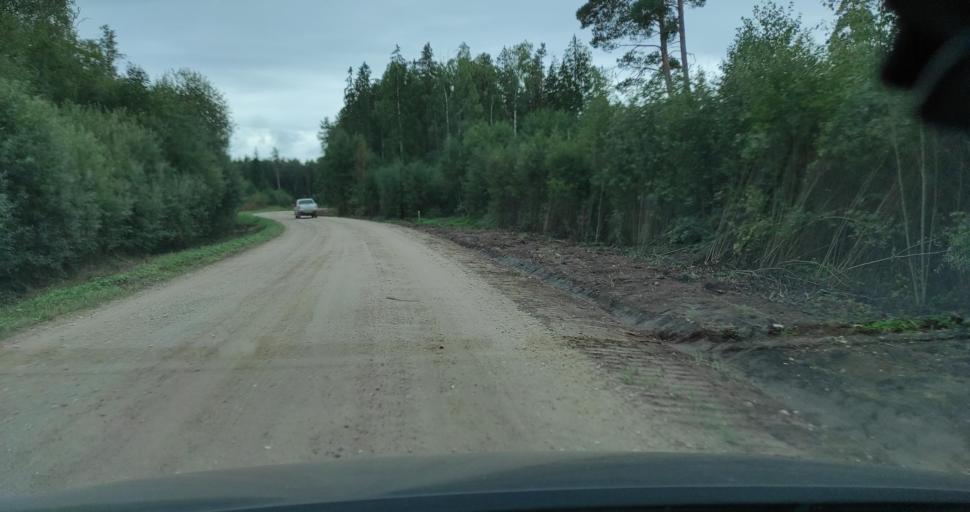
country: LV
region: Talsu Rajons
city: Stende
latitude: 57.0450
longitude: 22.3063
